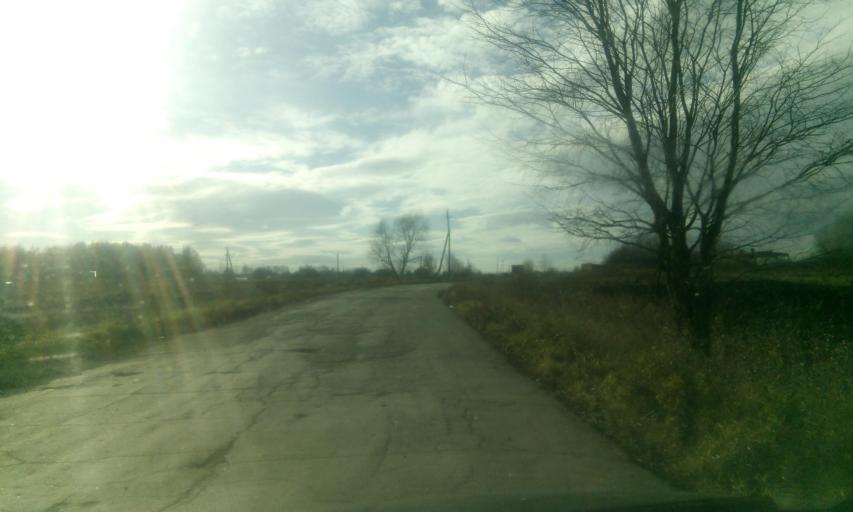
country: RU
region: Tula
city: Dubovka
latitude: 53.9430
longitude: 38.0349
